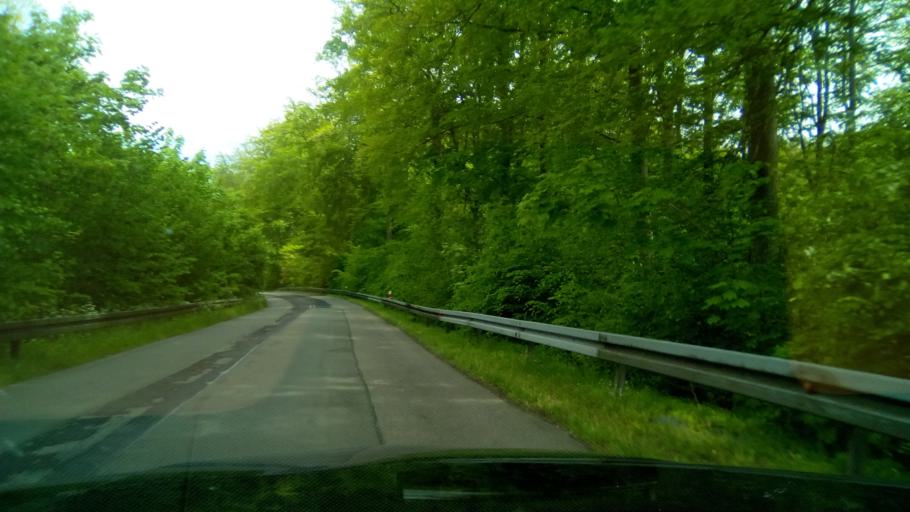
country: PL
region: Pomeranian Voivodeship
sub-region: Powiat leborski
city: Cewice
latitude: 54.3866
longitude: 17.6737
